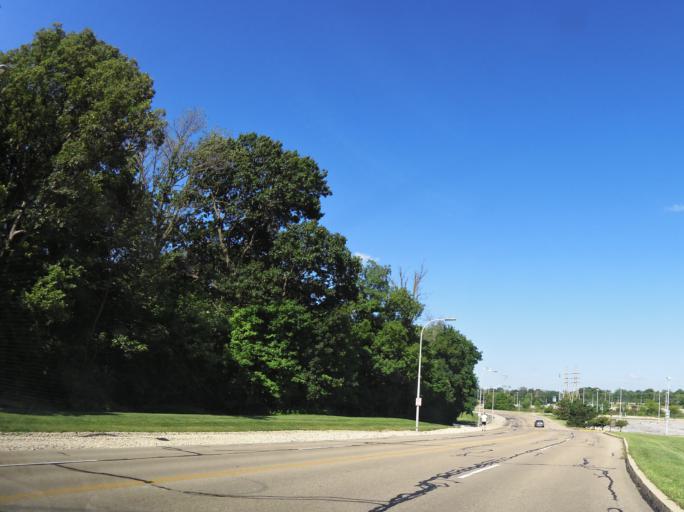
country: US
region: Ohio
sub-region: Greene County
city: Wright-Patterson AFB
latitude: 39.7838
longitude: -84.0530
